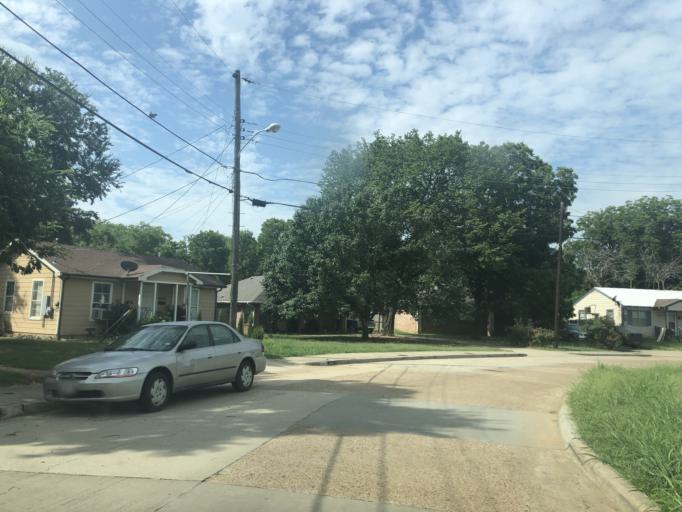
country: US
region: Texas
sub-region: Dallas County
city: Dallas
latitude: 32.8150
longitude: -96.8547
